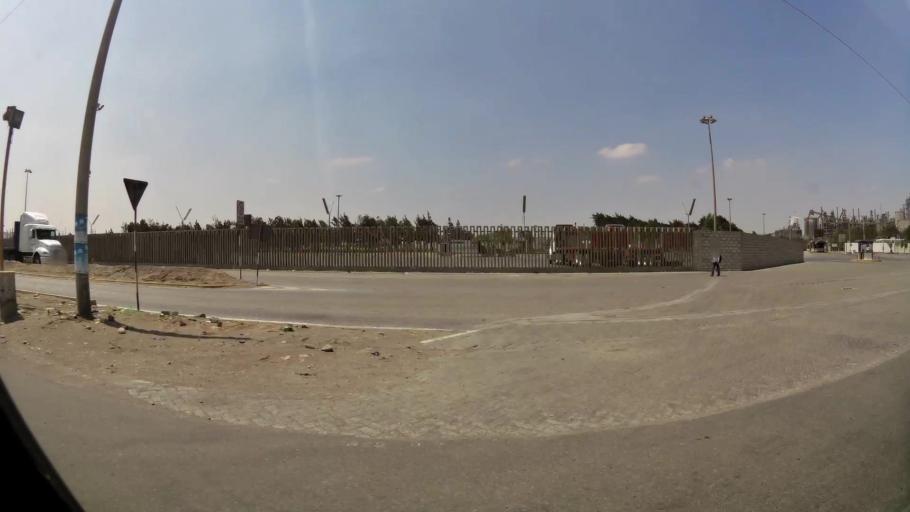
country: PE
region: La Libertad
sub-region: Provincia de Pacasmayo
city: Pacasmayo
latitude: -7.4020
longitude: -79.5586
